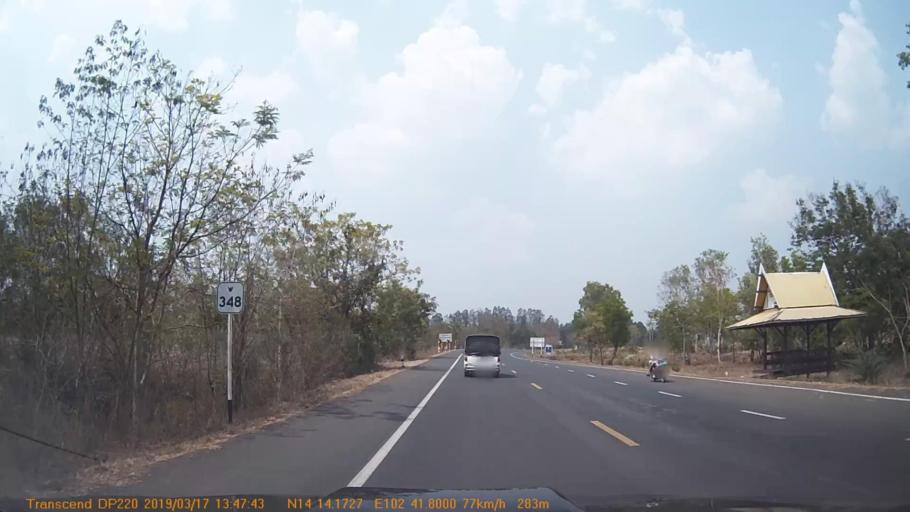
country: TH
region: Buriram
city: Non Din Daeng
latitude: 14.2365
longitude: 102.6966
